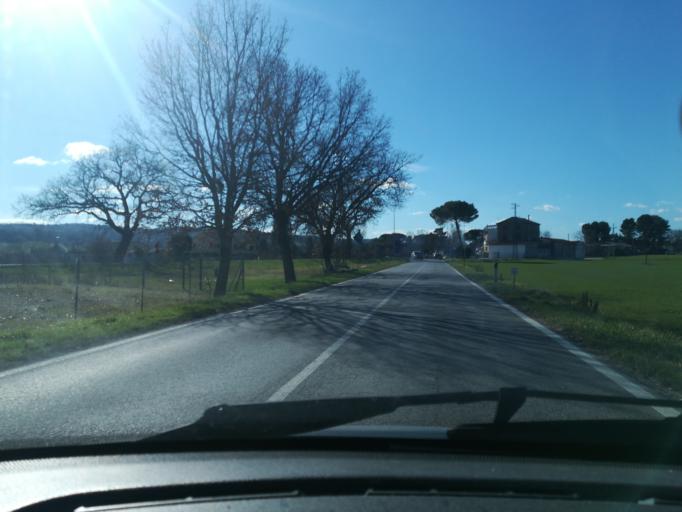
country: IT
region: The Marches
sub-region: Provincia di Macerata
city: Villa Potenza
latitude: 43.3312
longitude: 13.4253
